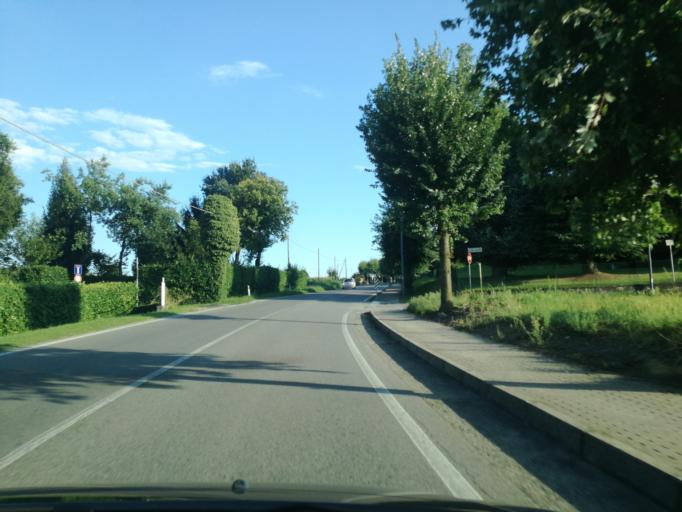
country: IT
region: Lombardy
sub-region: Provincia di Lecco
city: Arlate
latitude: 45.7276
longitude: 9.4419
